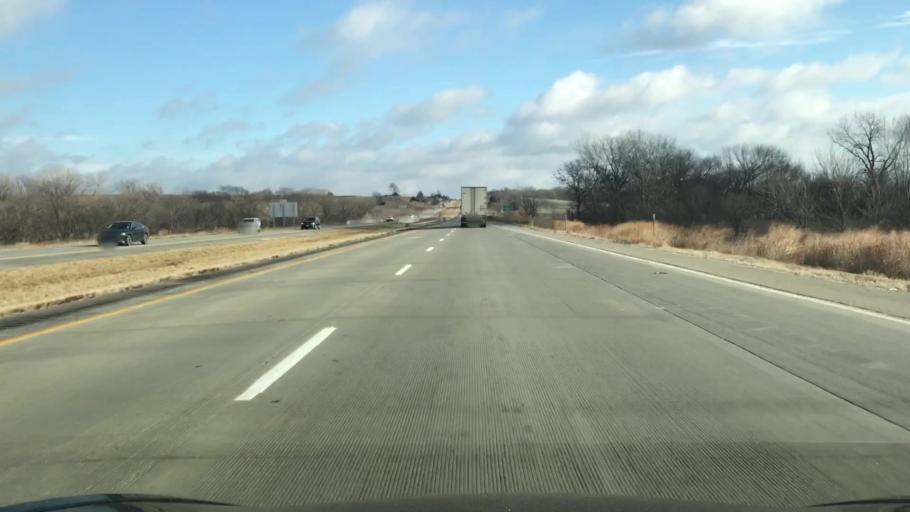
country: US
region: Iowa
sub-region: Cass County
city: Atlantic
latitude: 41.4970
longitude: -94.9372
